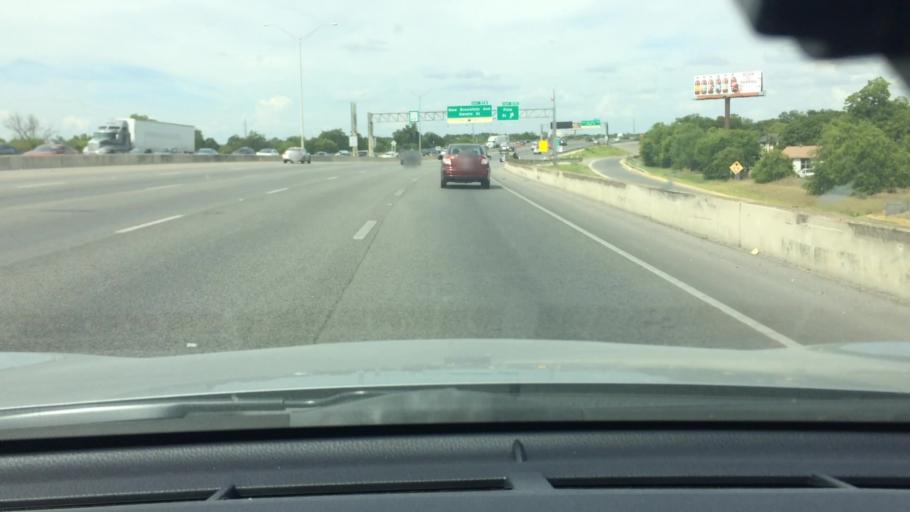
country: US
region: Texas
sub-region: Bexar County
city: San Antonio
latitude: 29.3985
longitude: -98.4735
